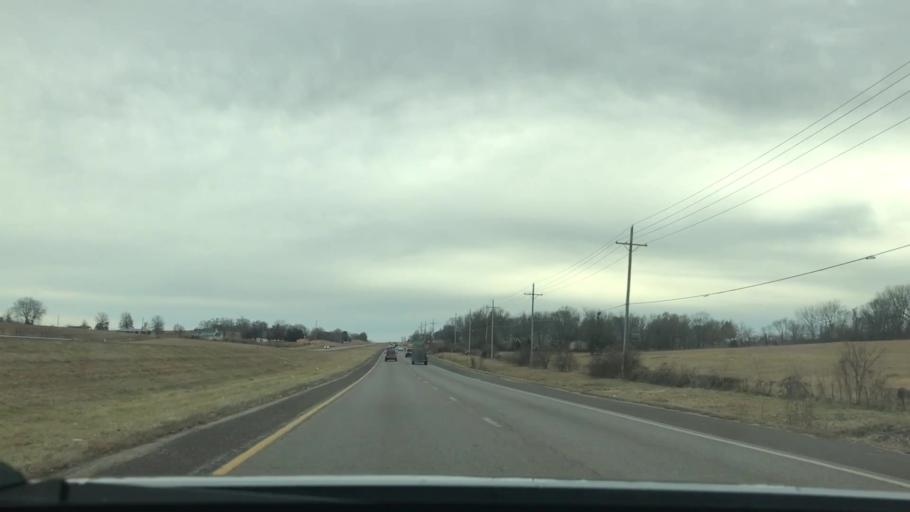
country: US
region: Kansas
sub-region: Leavenworth County
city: Lansing
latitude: 39.2211
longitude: -94.9003
